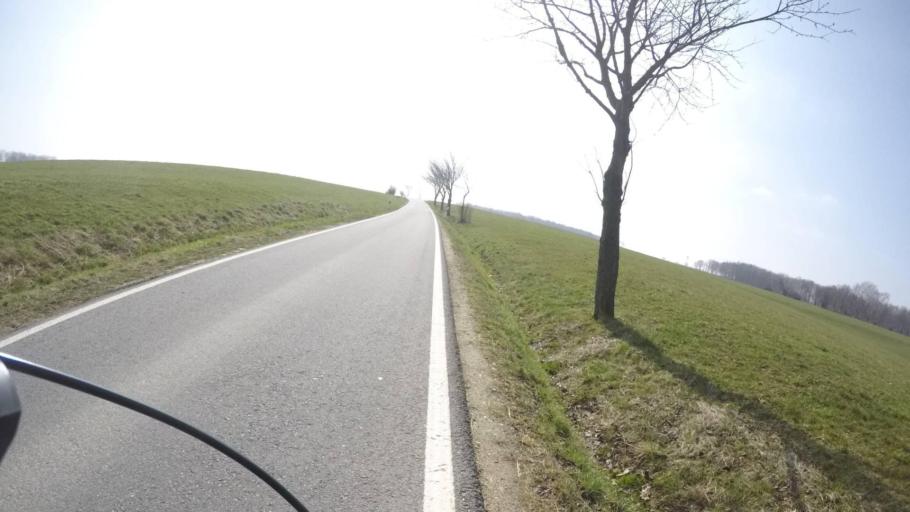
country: DE
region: Saxony
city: Niederfrohna
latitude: 50.8680
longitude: 12.6932
